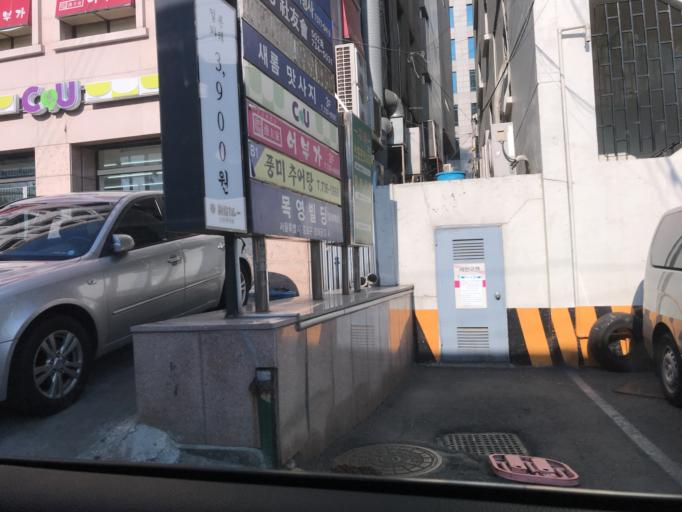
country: KR
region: Seoul
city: Seoul
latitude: 37.5703
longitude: 126.9720
